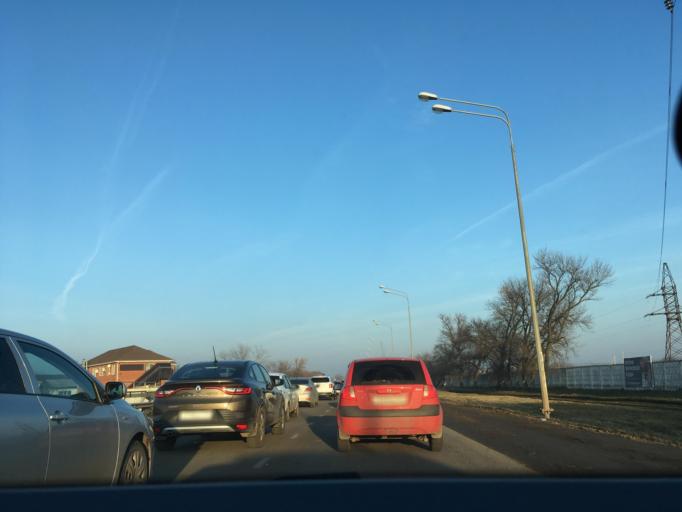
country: RU
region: Krasnodarskiy
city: Krasnodar
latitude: 45.1296
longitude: 39.0169
